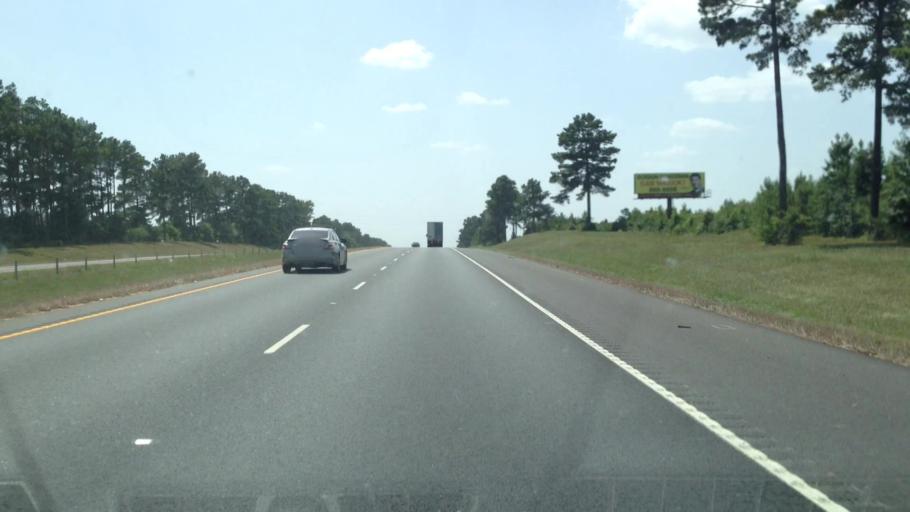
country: US
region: Louisiana
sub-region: Webster Parish
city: Minden
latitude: 32.5836
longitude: -93.2626
